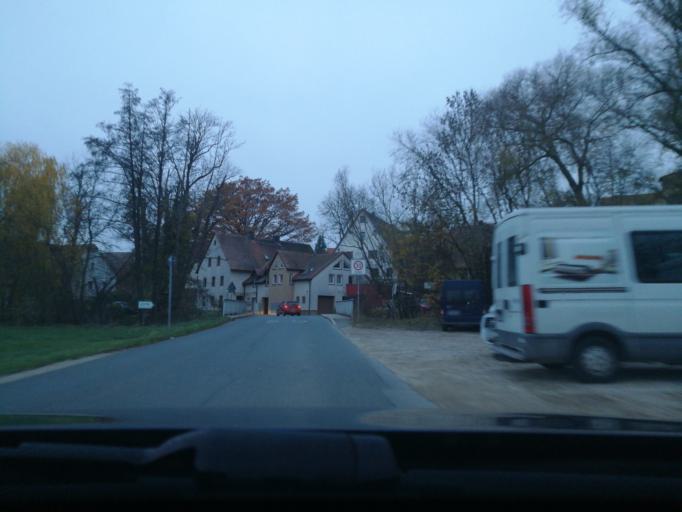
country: DE
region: Bavaria
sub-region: Regierungsbezirk Mittelfranken
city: Obermichelbach
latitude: 49.5081
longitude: 10.9382
